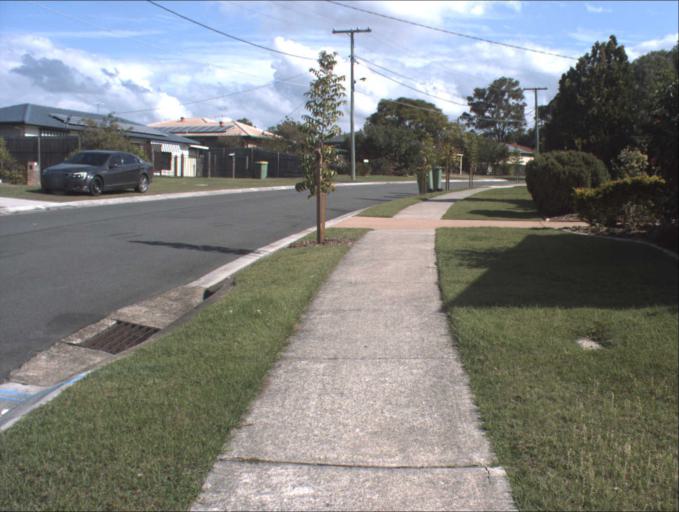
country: AU
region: Queensland
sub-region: Logan
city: Park Ridge South
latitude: -27.6935
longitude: 153.0159
